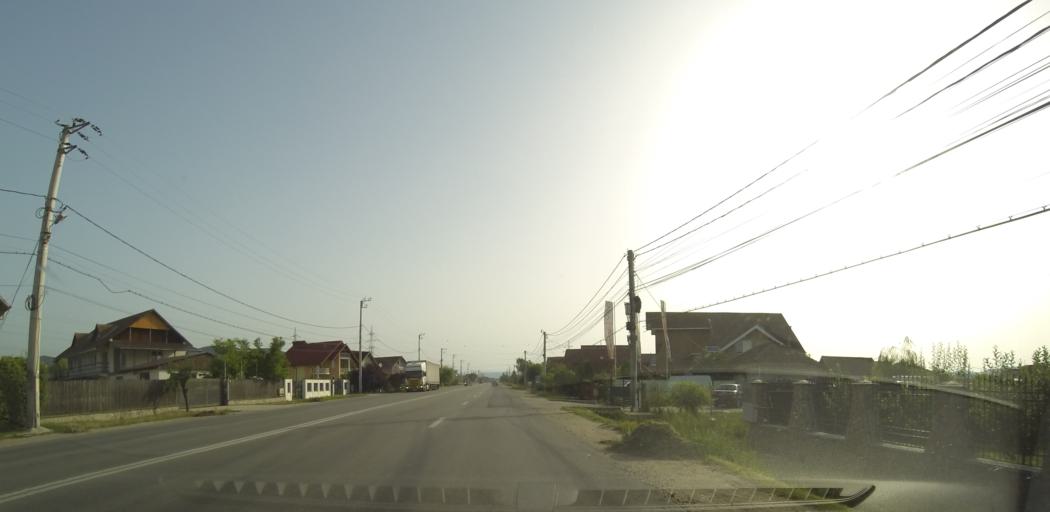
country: RO
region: Valcea
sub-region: Municipiul Ramnicu Valcea
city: Copacelu
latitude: 45.0579
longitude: 24.3324
